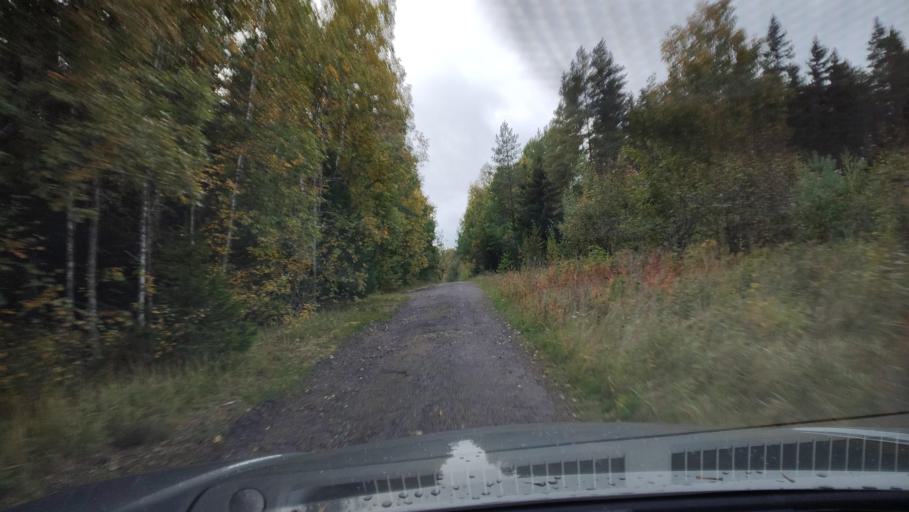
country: FI
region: Ostrobothnia
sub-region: Sydosterbotten
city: Kristinestad
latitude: 62.2708
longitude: 21.4491
